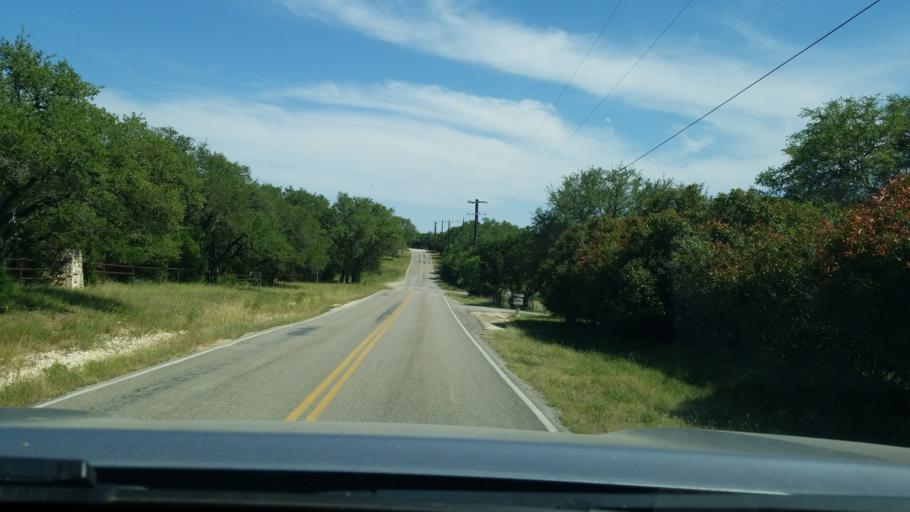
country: US
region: Texas
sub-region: Comal County
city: Bulverde
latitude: 29.7617
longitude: -98.5091
